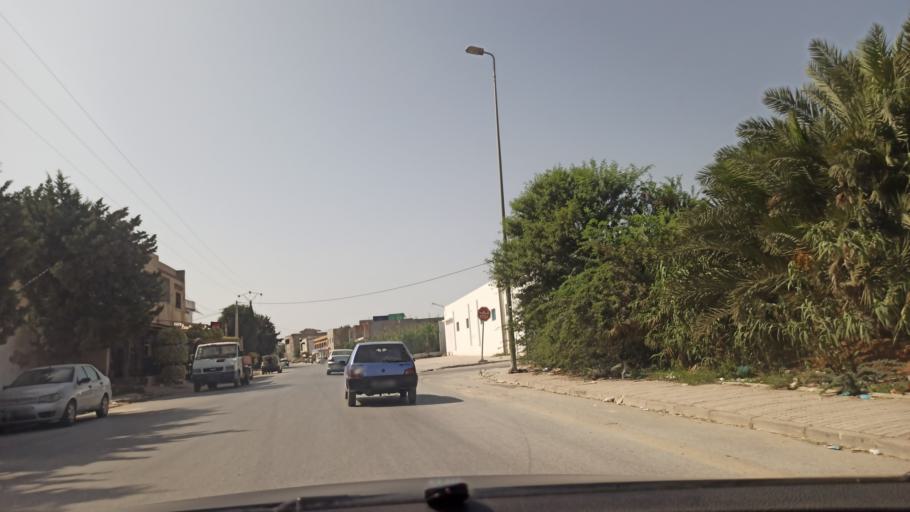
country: TN
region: Manouba
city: Manouba
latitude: 36.7580
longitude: 10.1045
